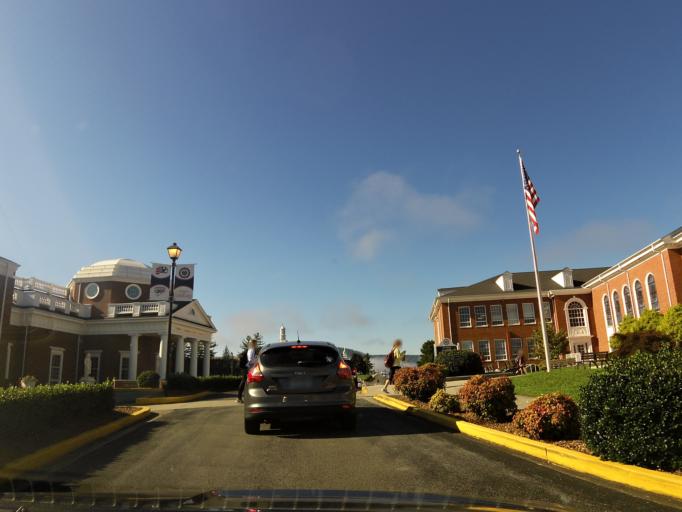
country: US
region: Kentucky
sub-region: Whitley County
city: Williamsburg
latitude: 36.7374
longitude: -84.1611
